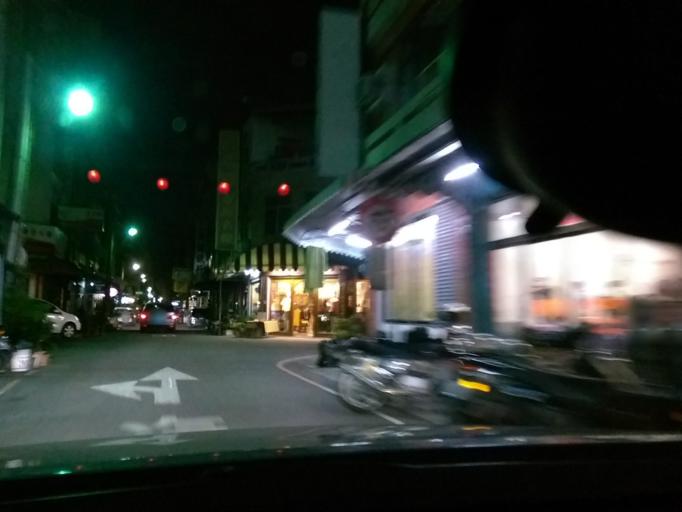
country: TW
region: Taiwan
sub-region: Chiayi
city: Jiayi Shi
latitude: 23.4764
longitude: 120.4477
